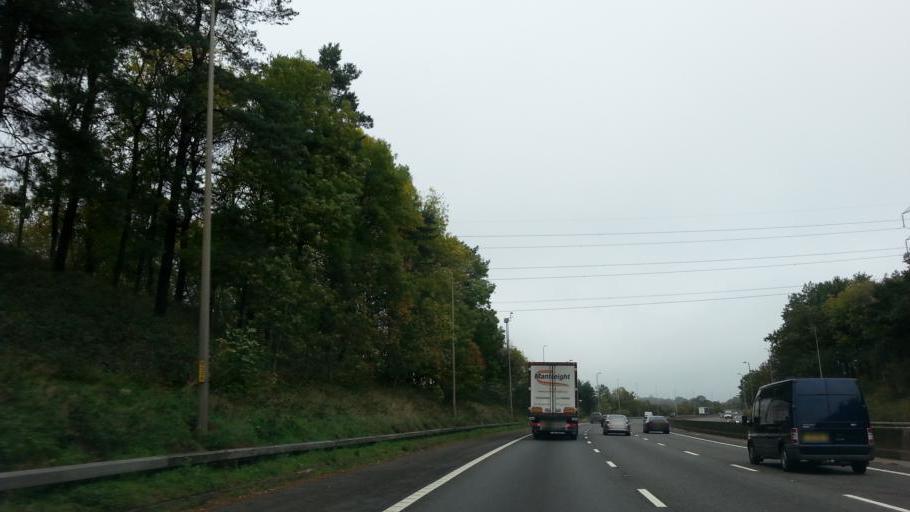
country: GB
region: England
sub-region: Dudley
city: Halesowen
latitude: 52.3941
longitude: -2.0536
